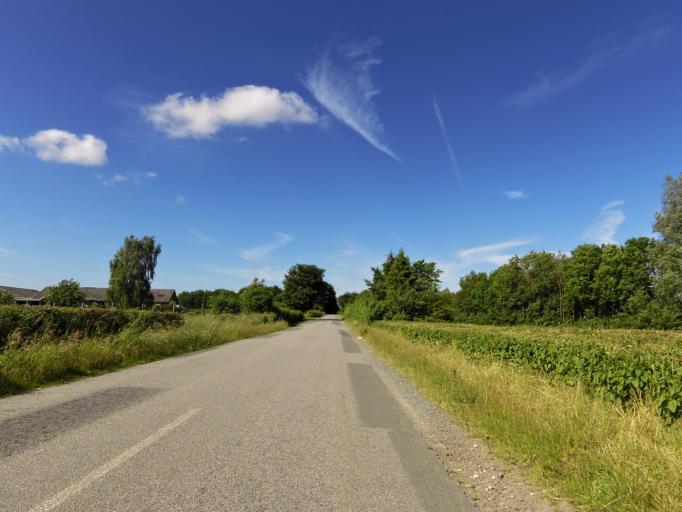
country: DK
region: South Denmark
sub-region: Aabenraa Kommune
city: Rodekro
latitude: 55.0607
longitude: 9.2980
